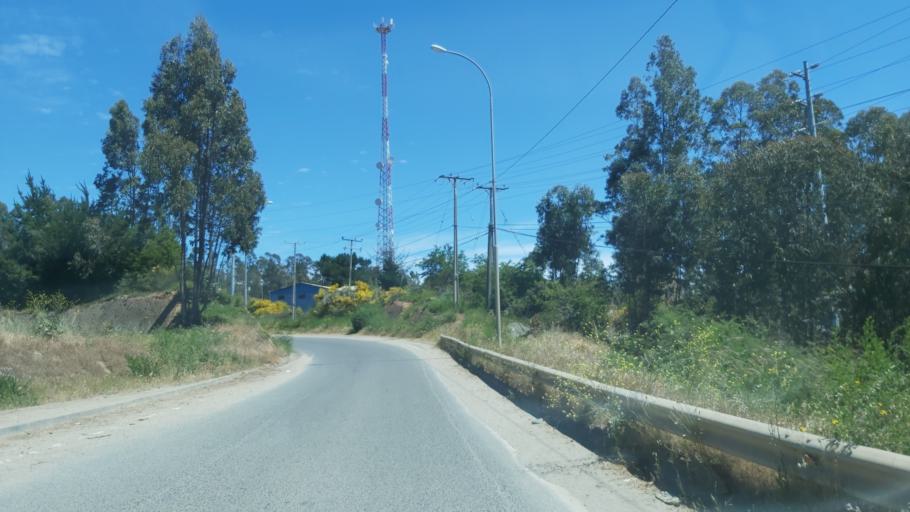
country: CL
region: Maule
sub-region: Provincia de Talca
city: Constitucion
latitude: -35.3654
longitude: -72.4022
